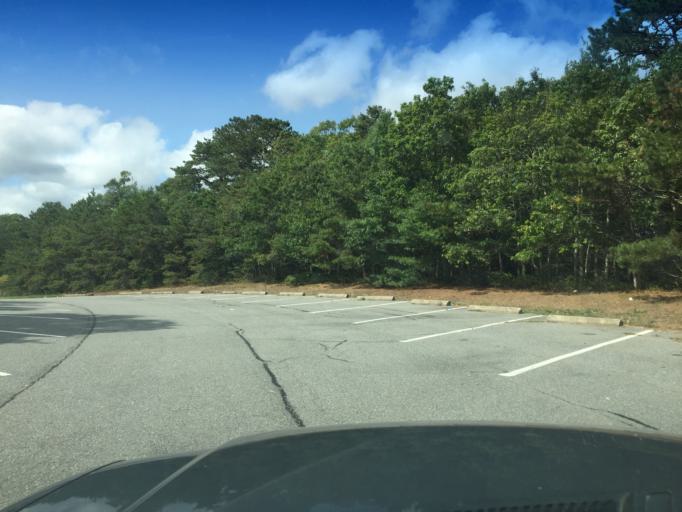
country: US
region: Massachusetts
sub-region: Plymouth County
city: White Island Shores
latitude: 41.7811
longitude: -70.6103
